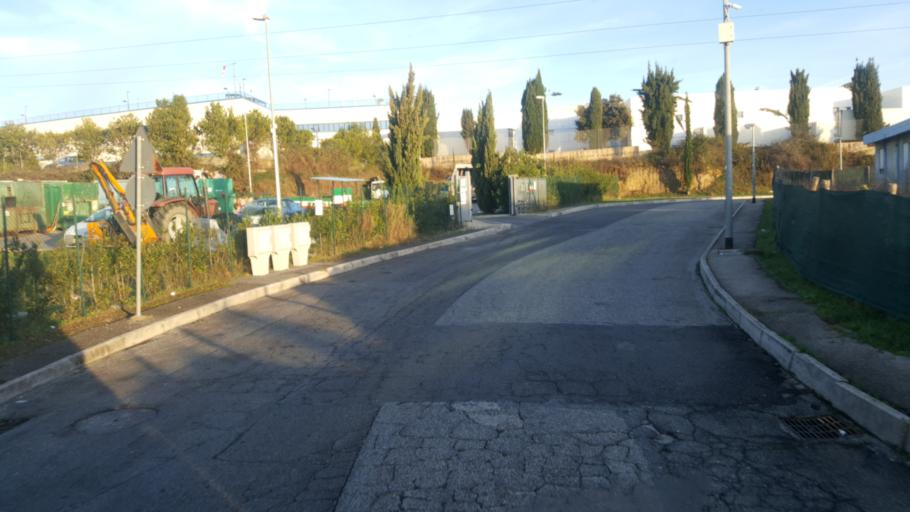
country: IT
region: Latium
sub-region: Citta metropolitana di Roma Capitale
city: Formello
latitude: 42.0527
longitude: 12.3993
